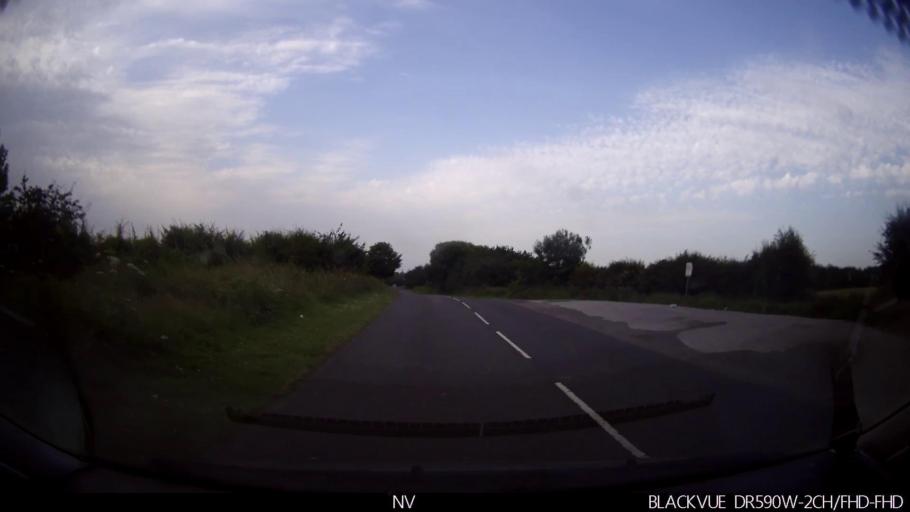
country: GB
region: England
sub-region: City of York
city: Copmanthorpe
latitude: 53.9421
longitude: -1.1425
